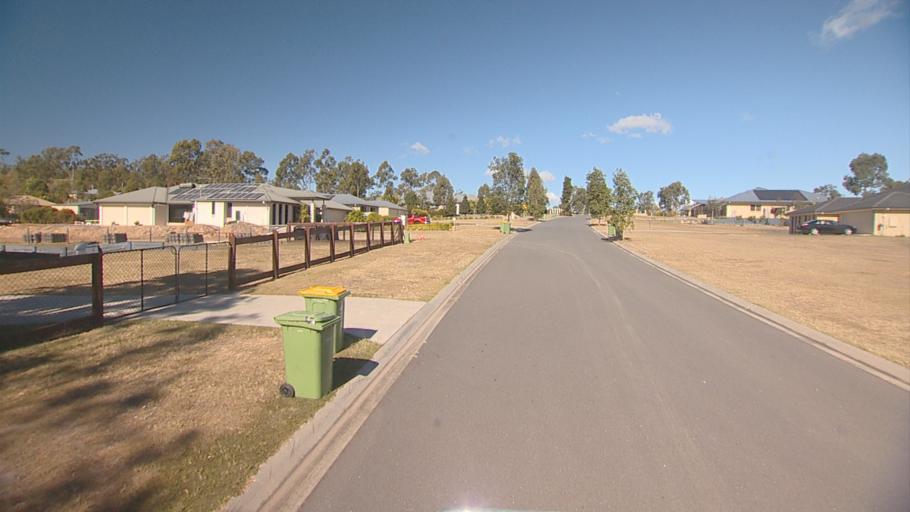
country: AU
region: Queensland
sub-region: Logan
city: North Maclean
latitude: -27.7585
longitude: 152.9500
